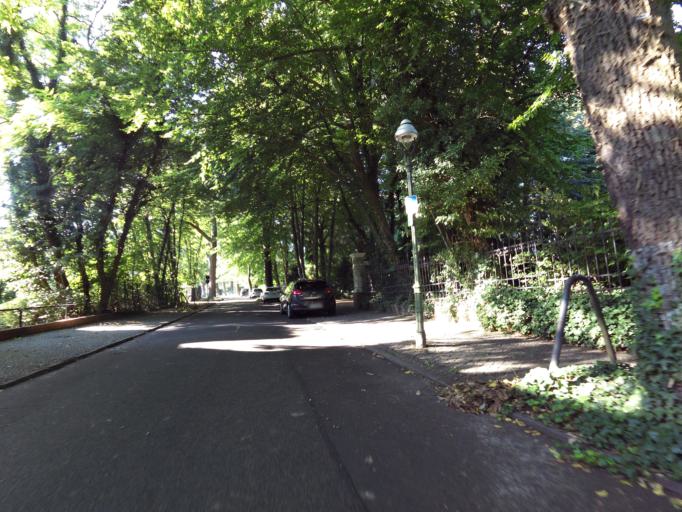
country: DE
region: Berlin
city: Kladow
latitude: 52.4488
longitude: 13.1683
